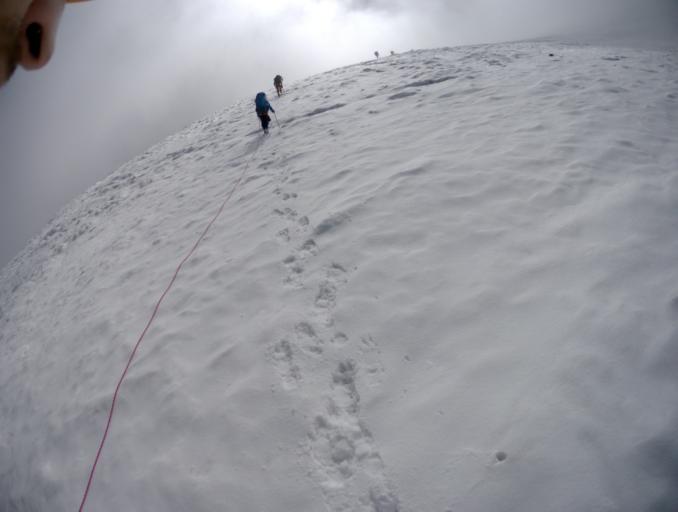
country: RU
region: Kabardino-Balkariya
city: Terskol
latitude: 43.3830
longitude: 42.4374
